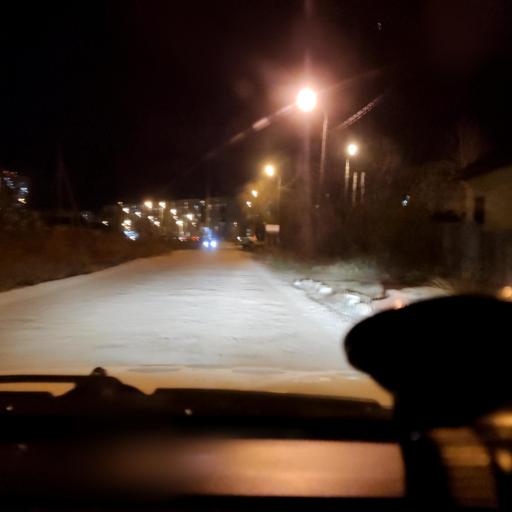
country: RU
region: Perm
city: Perm
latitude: 57.9757
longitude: 56.1924
